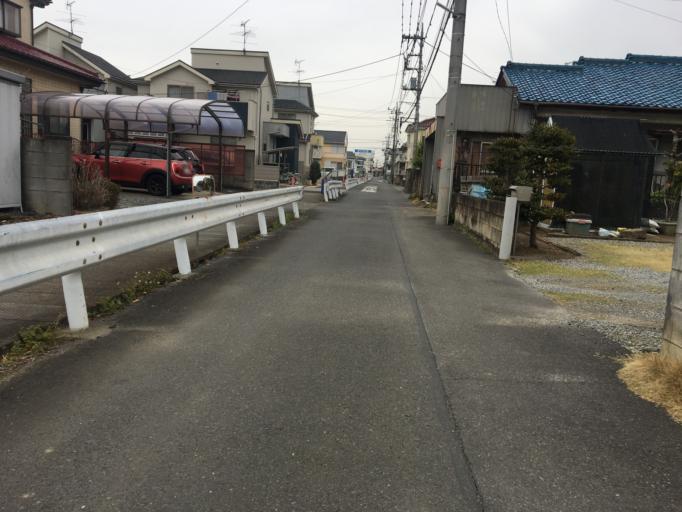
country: JP
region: Saitama
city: Kazo
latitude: 36.1208
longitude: 139.5934
